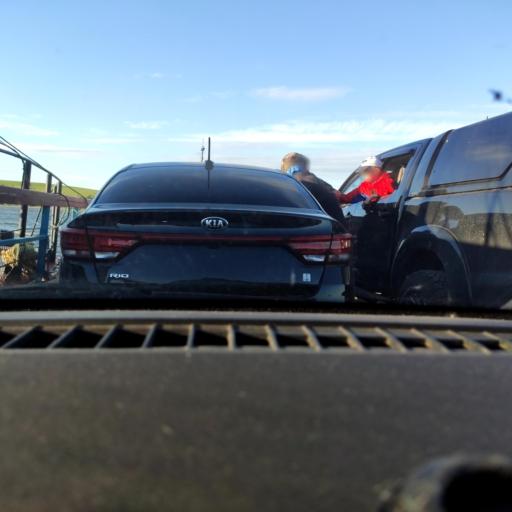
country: RU
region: Perm
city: Verkhnechusovskiye Gorodki
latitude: 58.1895
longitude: 57.1252
